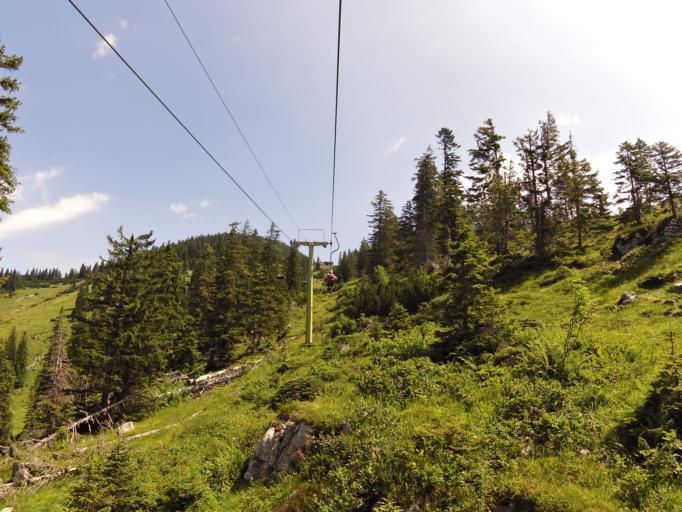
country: AT
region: Tyrol
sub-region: Politischer Bezirk Kitzbuhel
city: Waidring
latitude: 47.6674
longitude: 12.5975
